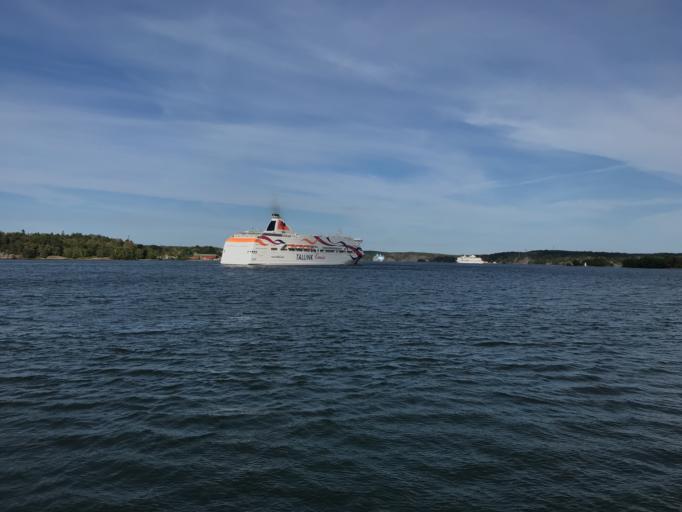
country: SE
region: Stockholm
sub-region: Nacka Kommun
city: Nacka
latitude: 59.3354
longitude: 18.1541
